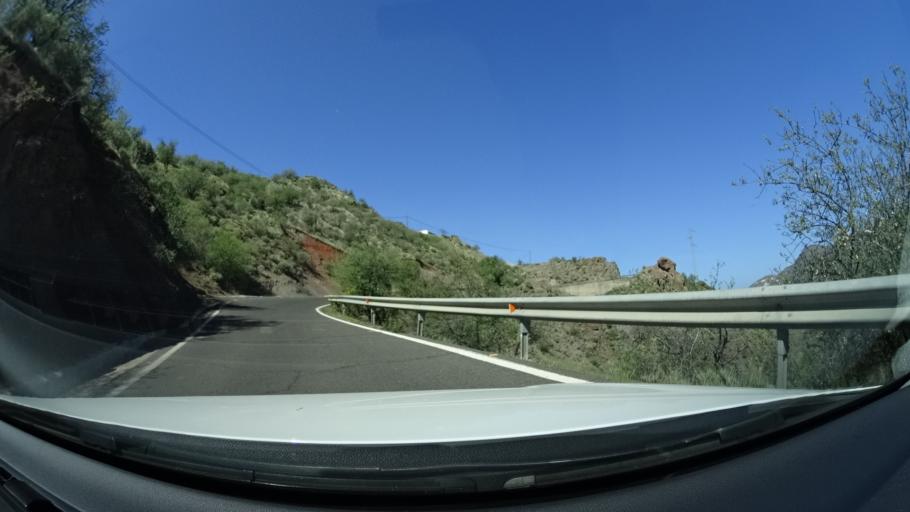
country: ES
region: Canary Islands
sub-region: Provincia de Las Palmas
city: Tejeda
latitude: 27.9873
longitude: -15.6273
